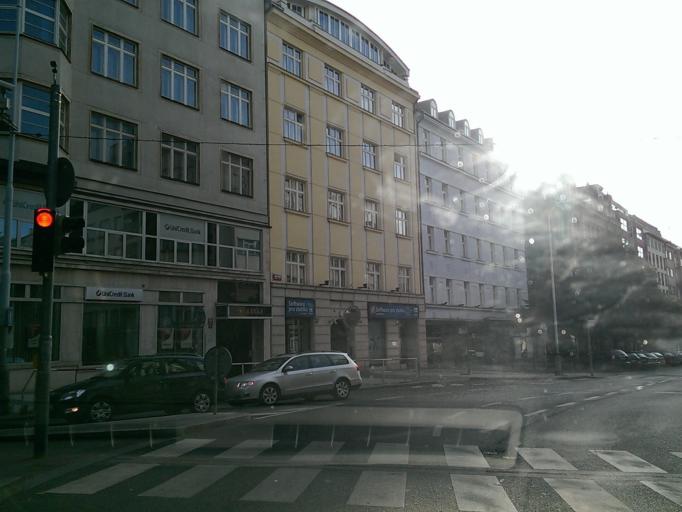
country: CZ
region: Praha
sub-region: Praha 1
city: Stare Mesto
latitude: 50.0758
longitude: 14.4353
